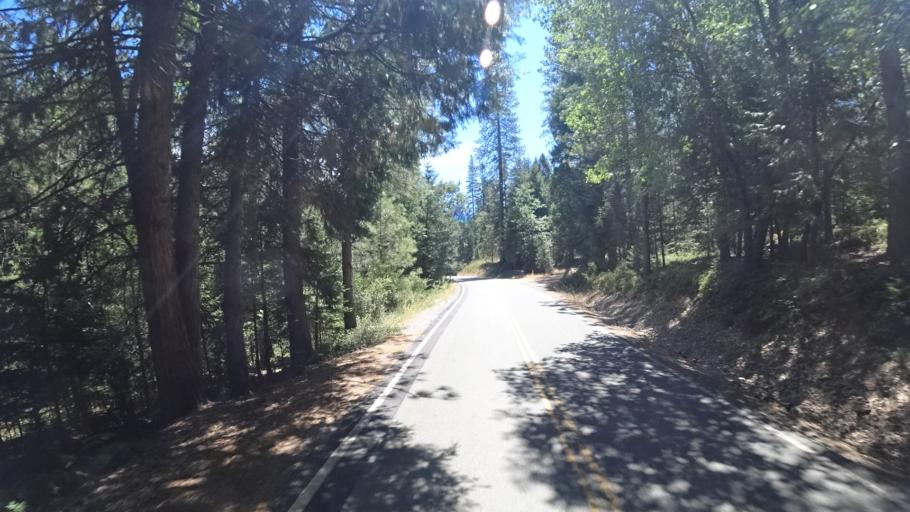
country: US
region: California
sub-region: Amador County
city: Pioneer
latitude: 38.3544
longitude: -120.5314
